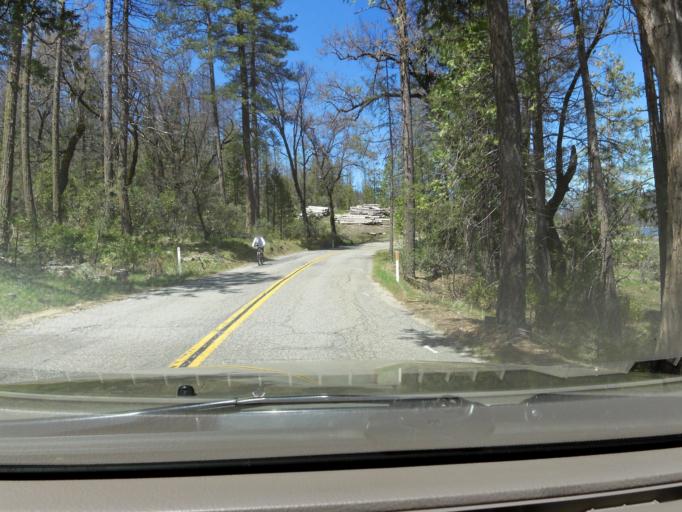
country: US
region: California
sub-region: Madera County
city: Oakhurst
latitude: 37.3160
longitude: -119.5731
